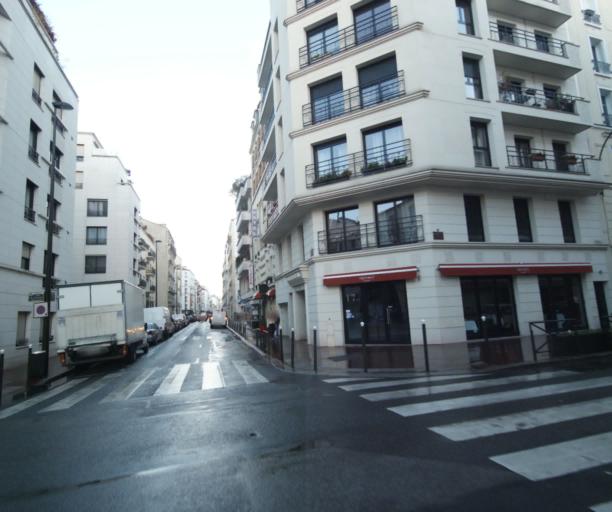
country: FR
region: Ile-de-France
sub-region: Departement des Hauts-de-Seine
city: Levallois-Perret
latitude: 48.8900
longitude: 2.2850
